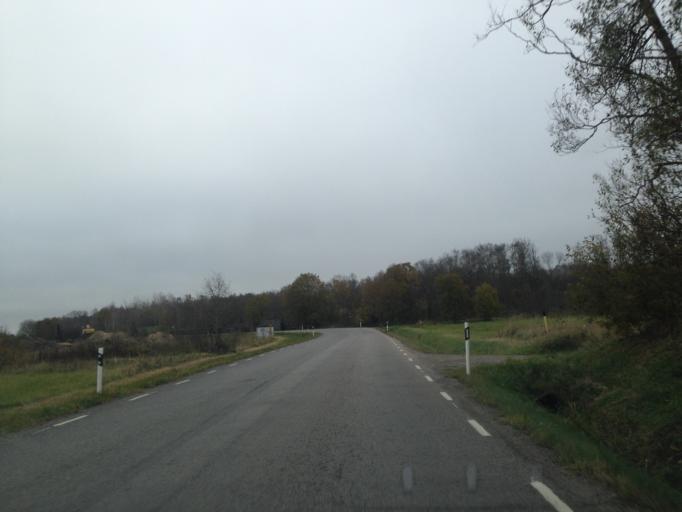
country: EE
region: Harju
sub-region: Saue linn
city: Saue
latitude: 59.3660
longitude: 24.5460
